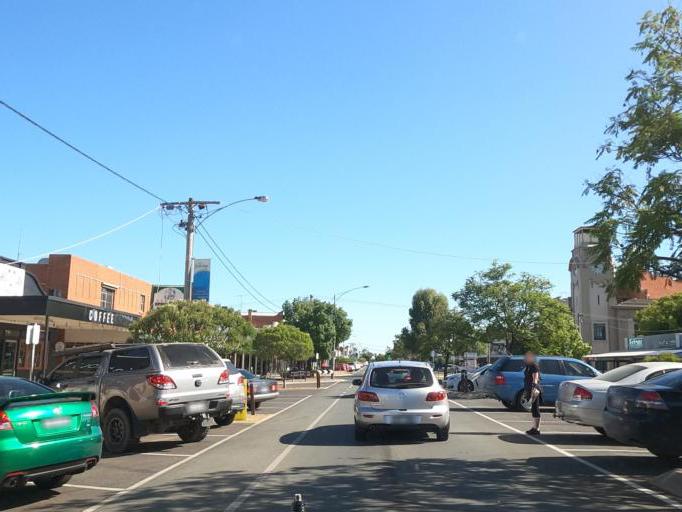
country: AU
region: Victoria
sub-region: Moira
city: Yarrawonga
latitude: -36.0137
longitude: 146.0044
